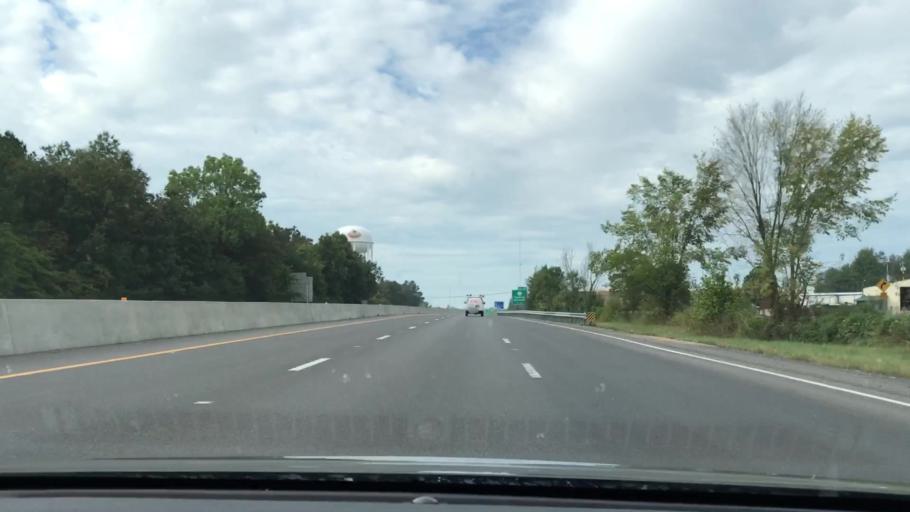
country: US
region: Kentucky
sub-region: Graves County
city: Mayfield
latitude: 36.7645
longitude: -88.6468
